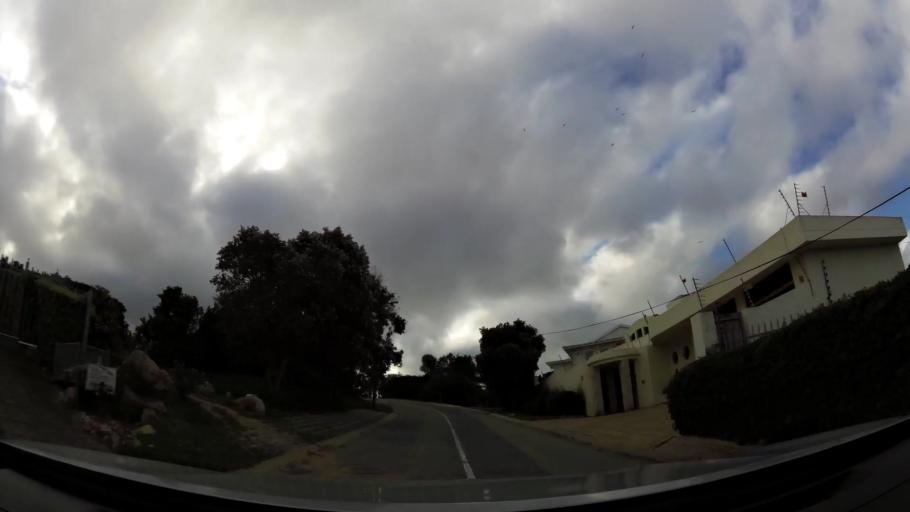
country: ZA
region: Western Cape
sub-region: Eden District Municipality
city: Plettenberg Bay
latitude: -34.0577
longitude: 23.3768
